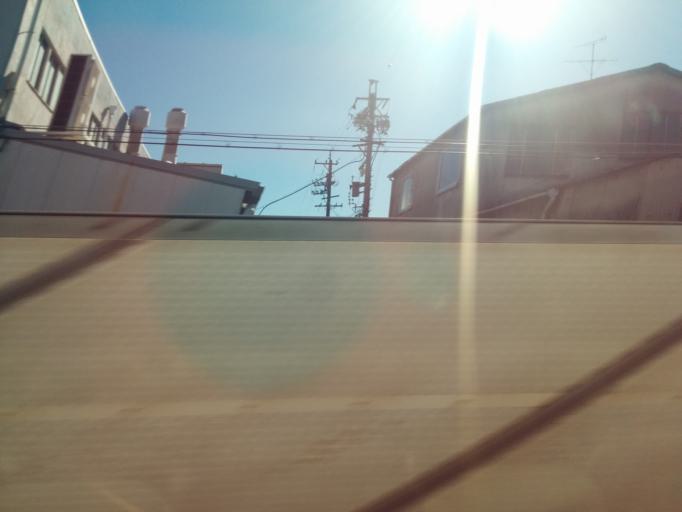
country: JP
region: Aichi
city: Nagoya-shi
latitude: 35.0895
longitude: 136.9297
